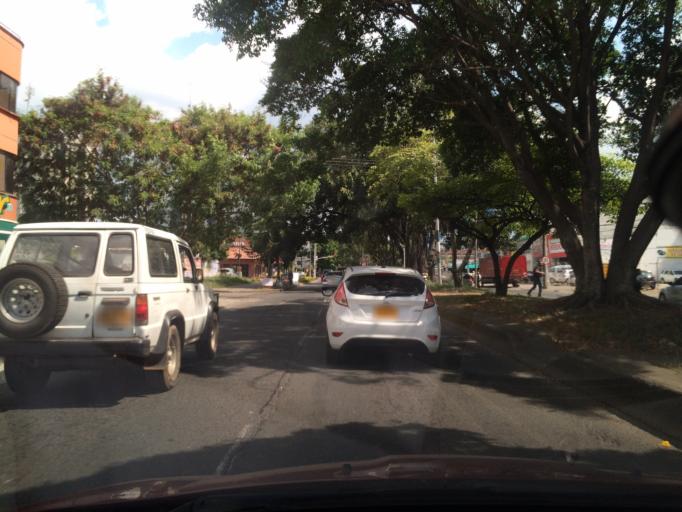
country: CO
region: Valle del Cauca
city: Cali
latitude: 3.4232
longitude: -76.5412
